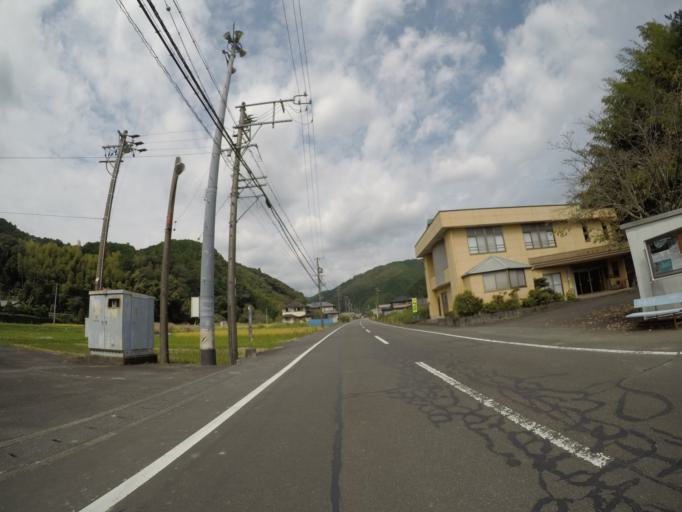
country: JP
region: Shizuoka
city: Shimada
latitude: 34.8677
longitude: 138.1828
